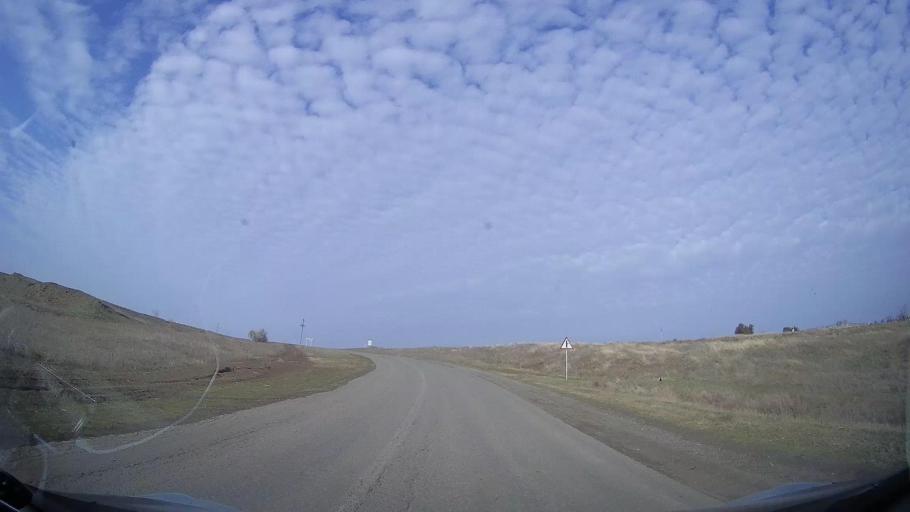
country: RU
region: Rostov
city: Gigant
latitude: 46.8442
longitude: 41.3304
